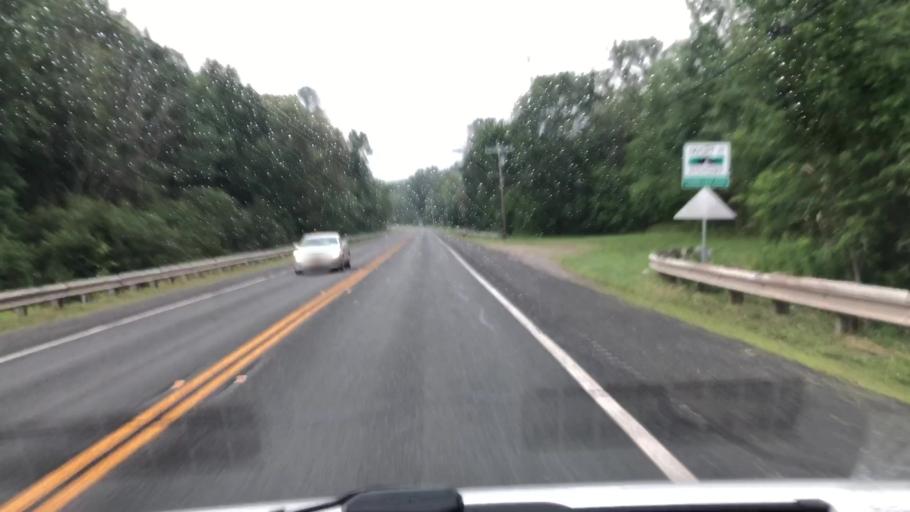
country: US
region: Massachusetts
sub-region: Berkshire County
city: Lanesborough
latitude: 42.6079
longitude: -73.2359
